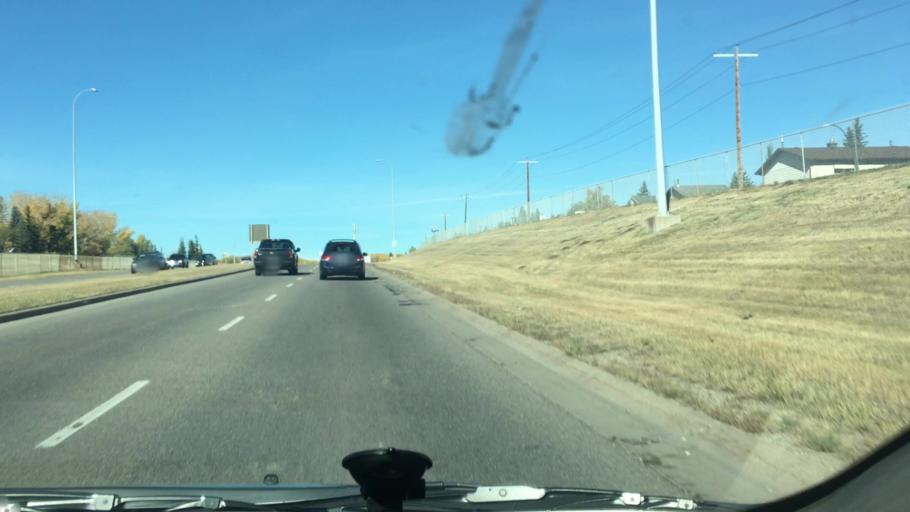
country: CA
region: Alberta
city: Calgary
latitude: 51.1173
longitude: -114.1592
